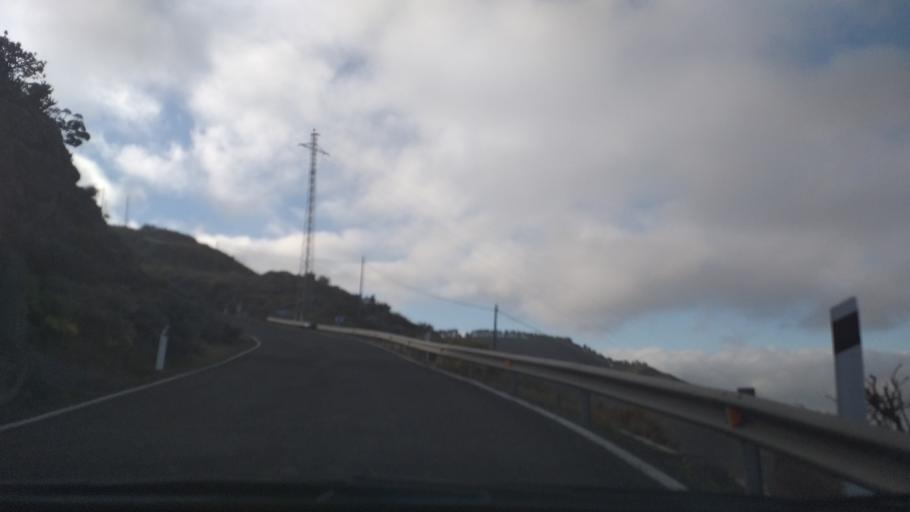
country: ES
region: Canary Islands
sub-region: Provincia de Las Palmas
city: Valsequillo de Gran Canaria
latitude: 27.9582
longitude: -15.4980
